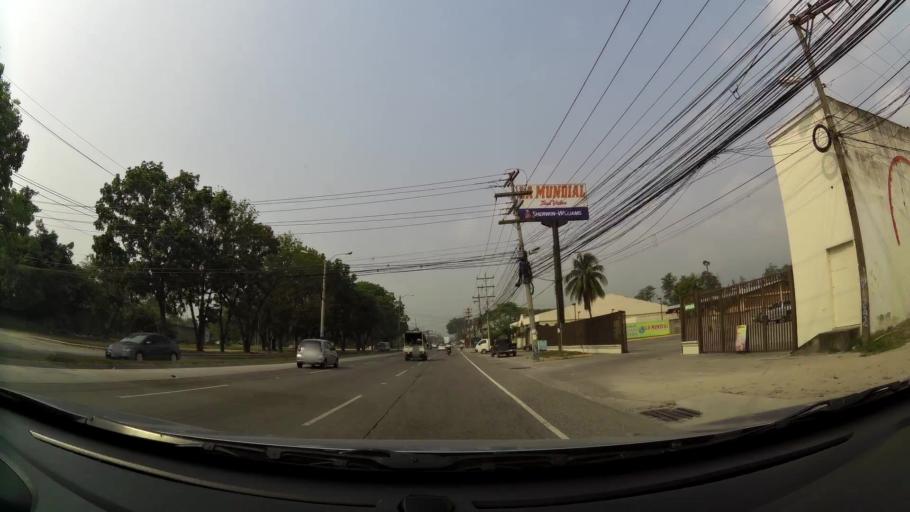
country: HN
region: Cortes
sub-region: San Pedro Sula
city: Pena Blanca
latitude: 15.5365
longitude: -88.0175
